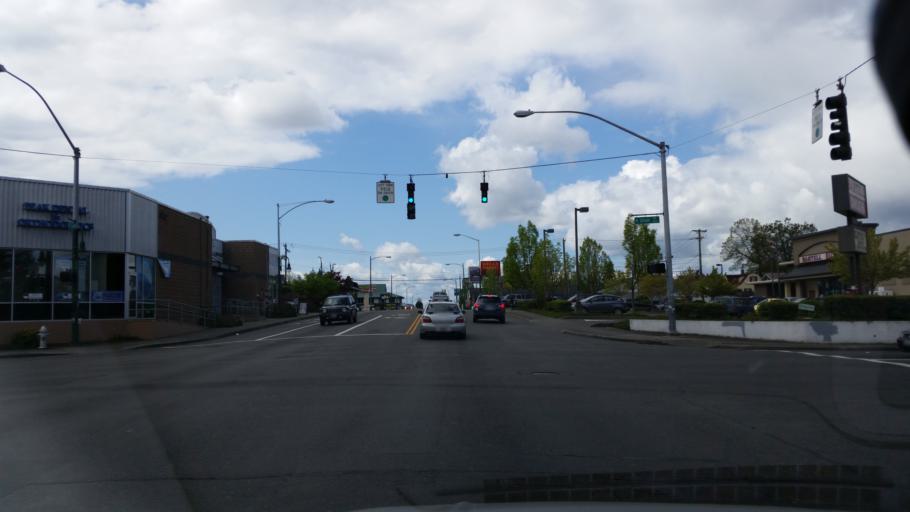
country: US
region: Washington
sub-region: Pierce County
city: Fircrest
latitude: 47.2553
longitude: -122.4833
